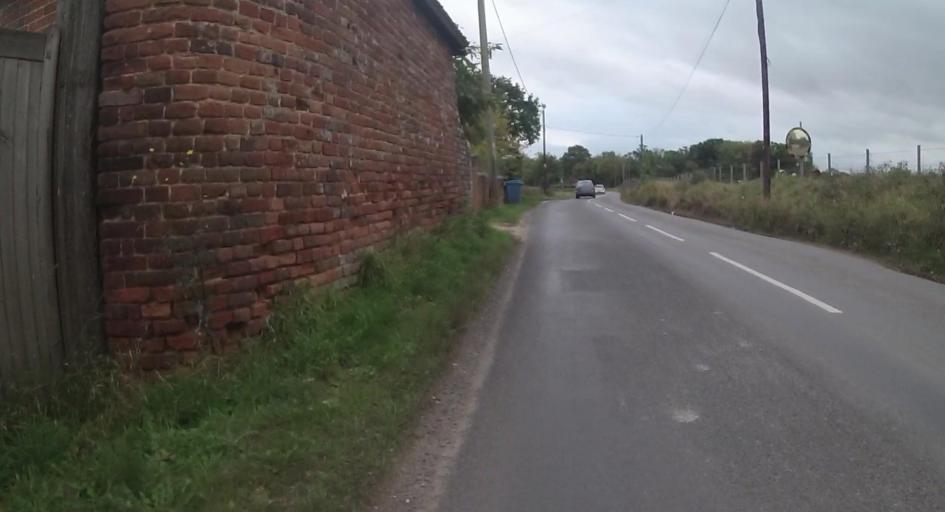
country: GB
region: England
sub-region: Hampshire
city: Fleet
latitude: 51.2565
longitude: -0.8662
